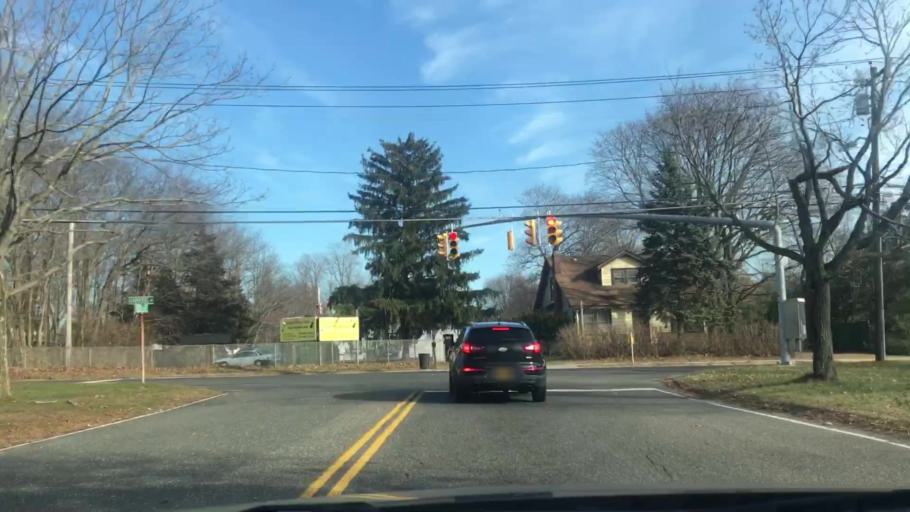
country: US
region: New York
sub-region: Suffolk County
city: Ronkonkoma
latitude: 40.8328
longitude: -73.1092
